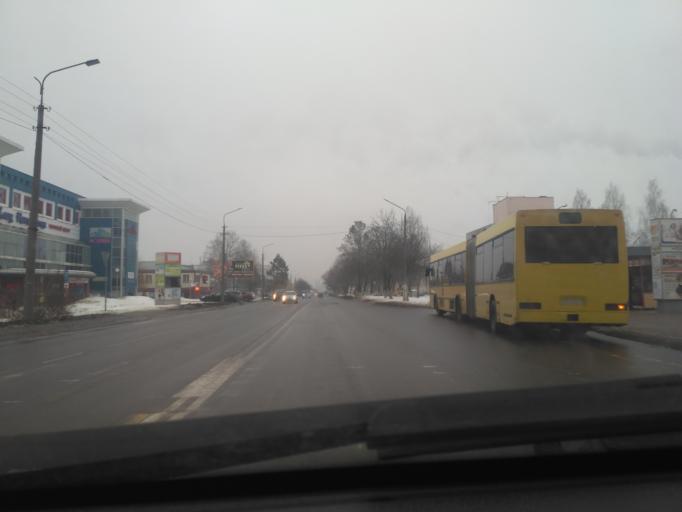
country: BY
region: Minsk
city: Horad Barysaw
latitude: 54.2079
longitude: 28.4894
